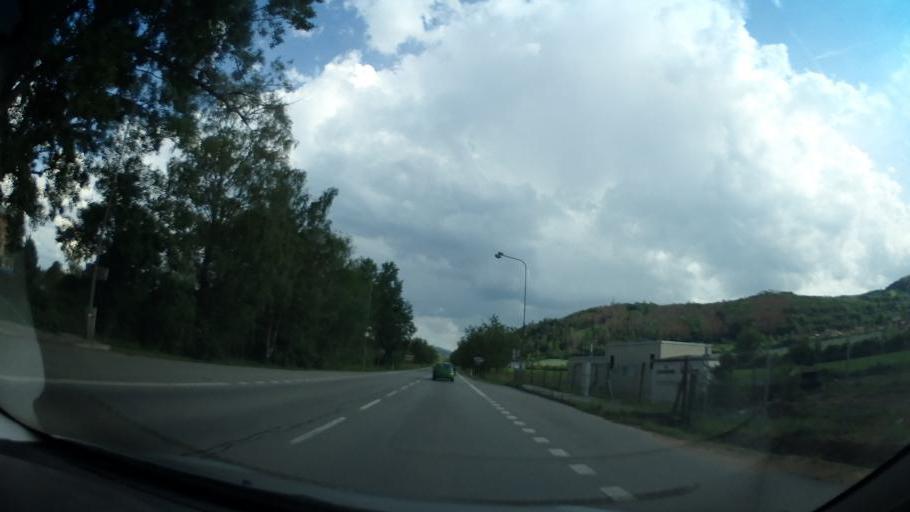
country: CZ
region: South Moravian
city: Predklasteri
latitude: 49.3514
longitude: 16.4080
